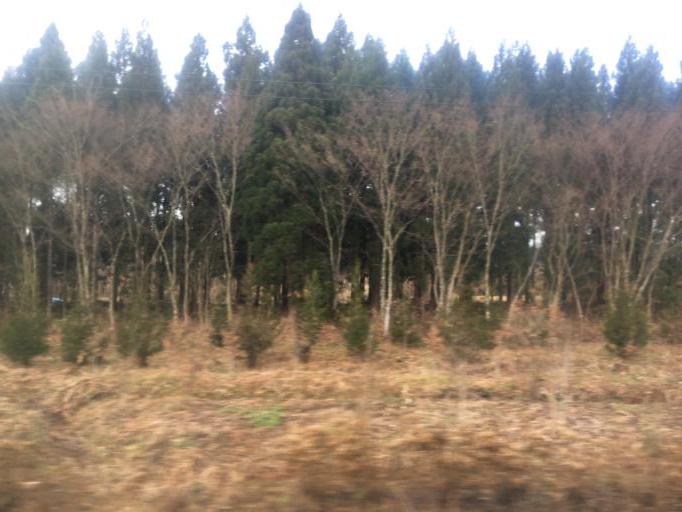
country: JP
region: Akita
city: Takanosu
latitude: 40.2421
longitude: 140.3874
